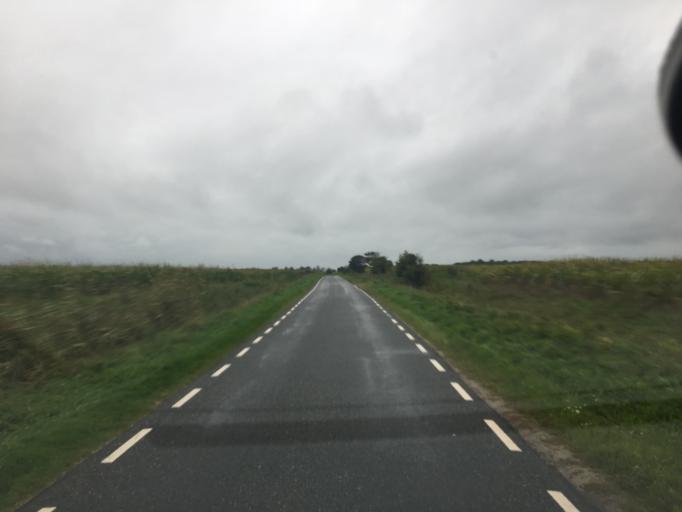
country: DE
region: Schleswig-Holstein
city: Ellhoft
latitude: 54.9359
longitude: 8.9394
